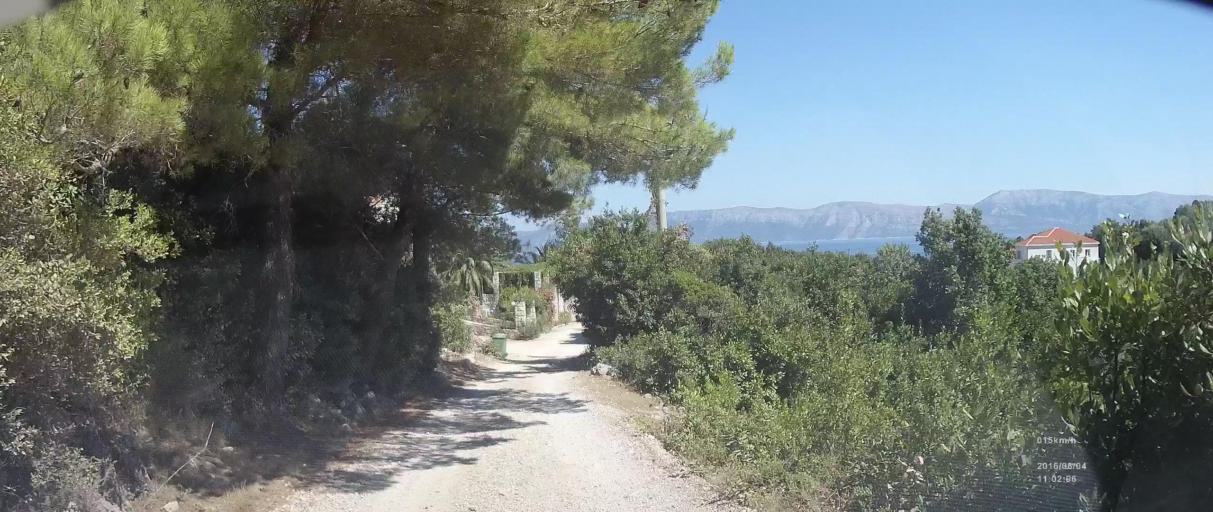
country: HR
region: Dubrovacko-Neretvanska
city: Blato
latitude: 42.7750
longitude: 17.4647
